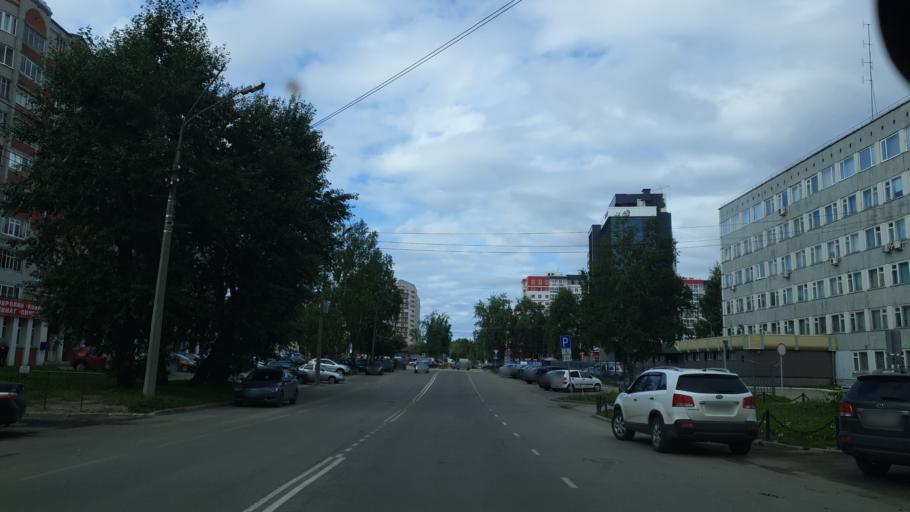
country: RU
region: Komi Republic
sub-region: Syktyvdinskiy Rayon
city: Syktyvkar
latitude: 61.6737
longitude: 50.8247
